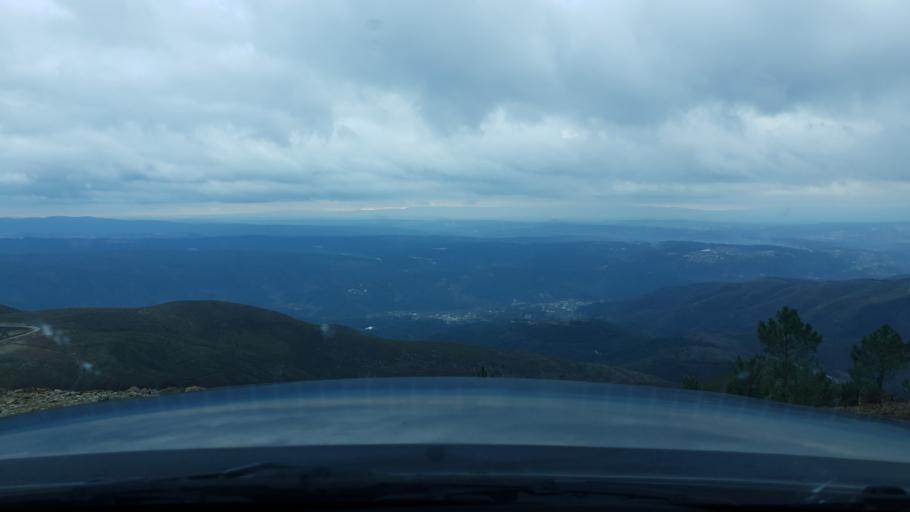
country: PT
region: Viseu
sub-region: Sao Pedro do Sul
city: Sao Pedro do Sul
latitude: 40.8646
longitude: -8.0821
